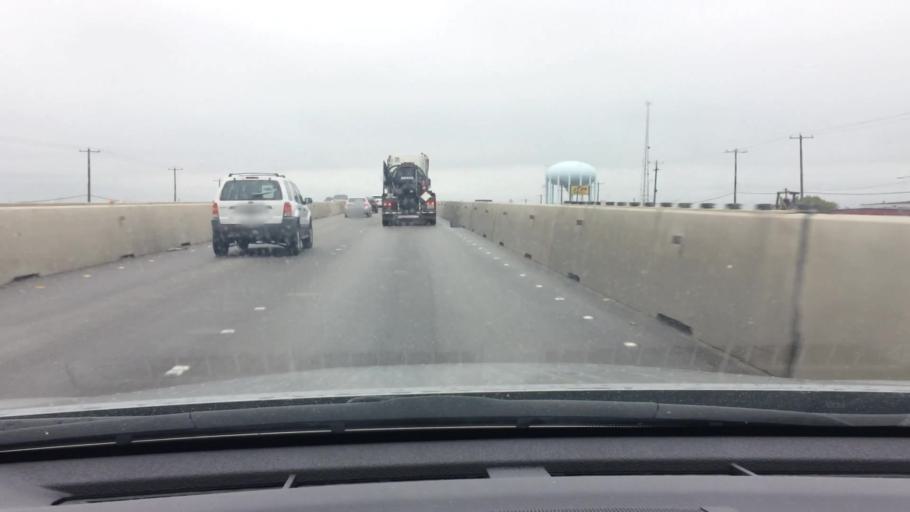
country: US
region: Texas
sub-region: Bexar County
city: Kirby
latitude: 29.4488
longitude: -98.3482
